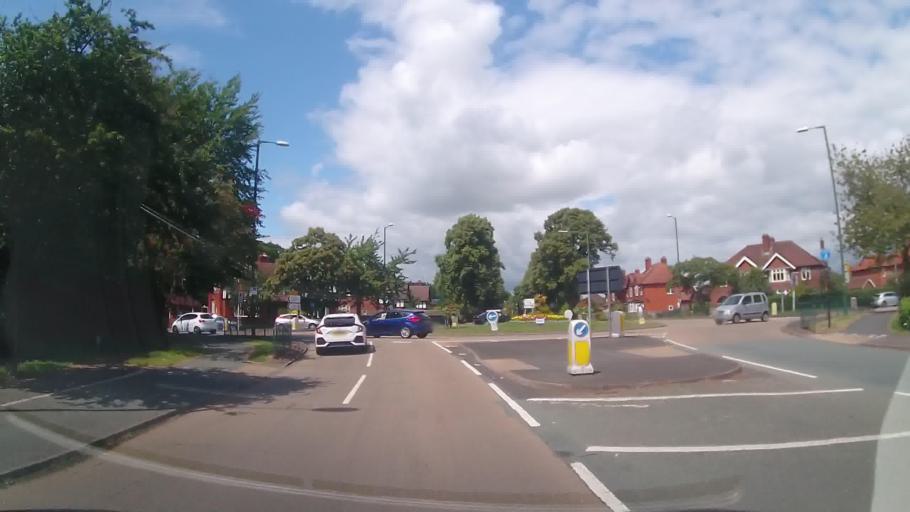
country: GB
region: England
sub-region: Shropshire
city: Shrewsbury
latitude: 52.7076
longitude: -2.7790
